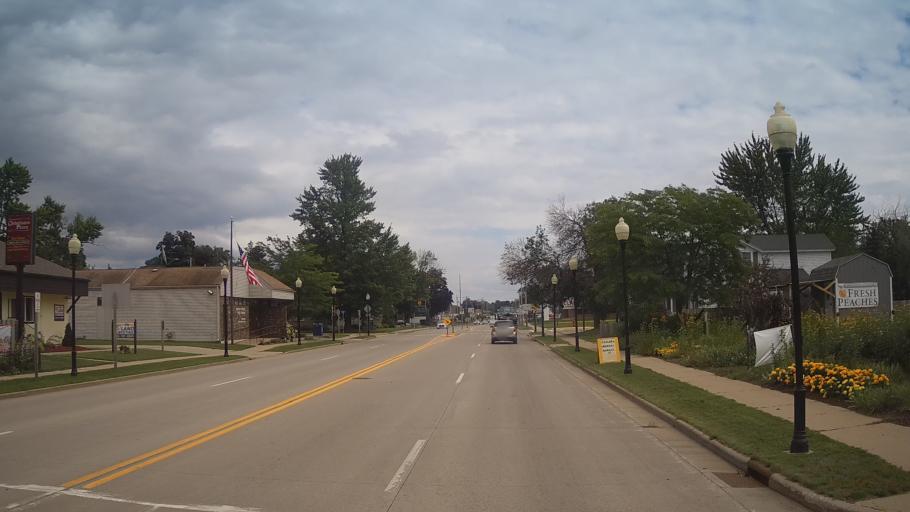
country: US
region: Wisconsin
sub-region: Waushara County
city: Wautoma
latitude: 44.0748
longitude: -89.2891
